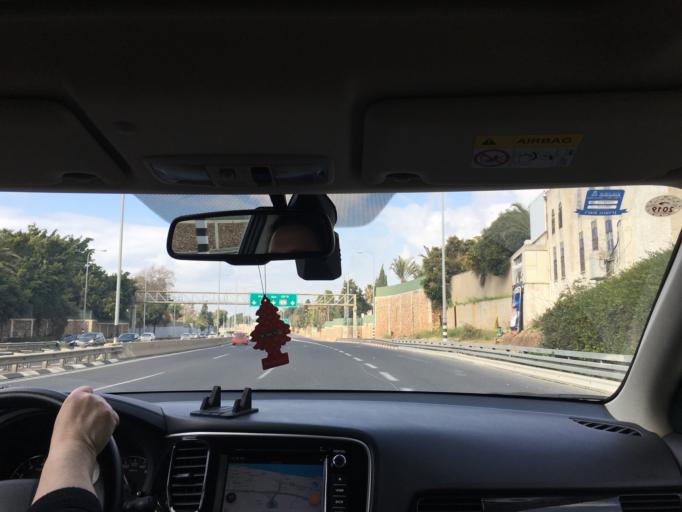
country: IL
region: Tel Aviv
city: Kefar Shemaryahu
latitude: 32.1746
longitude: 34.8159
